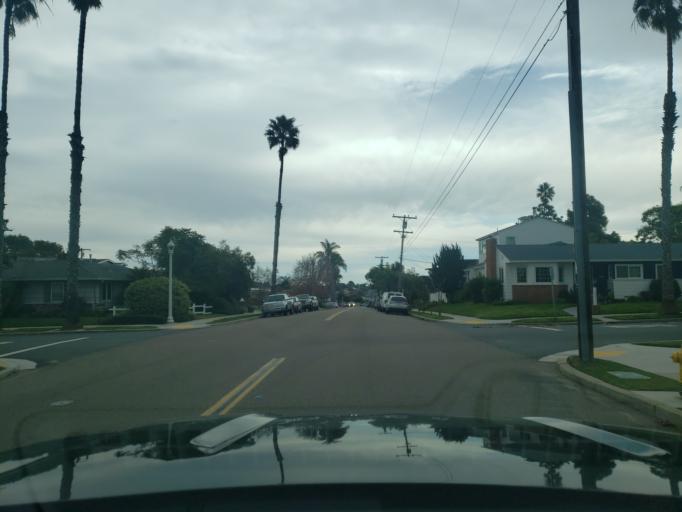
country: US
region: California
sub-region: San Diego County
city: Coronado
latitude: 32.7257
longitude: -117.2468
